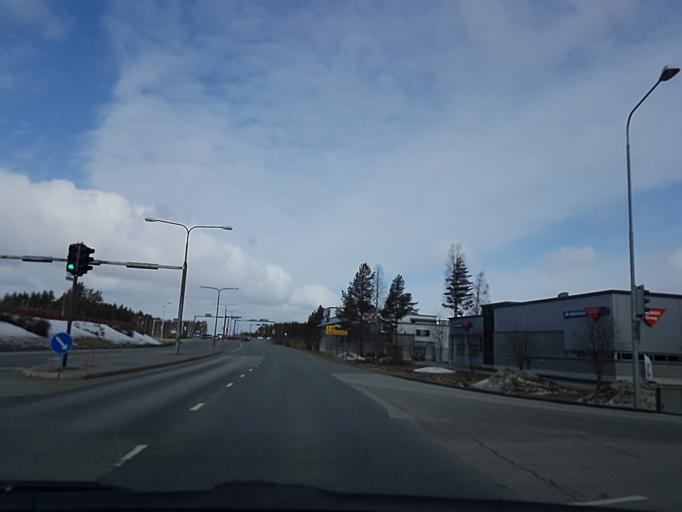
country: FI
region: North Karelia
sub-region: Joensuu
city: Joensuu
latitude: 62.6138
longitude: 29.7380
